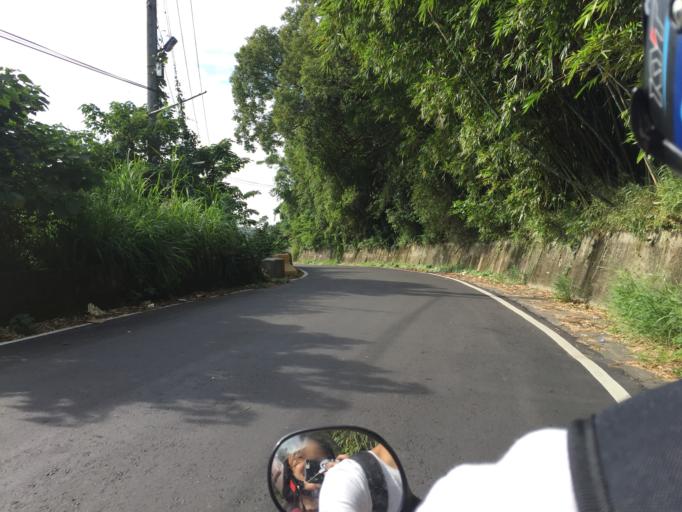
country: TW
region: Taiwan
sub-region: Hsinchu
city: Hsinchu
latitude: 24.7711
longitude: 120.9373
